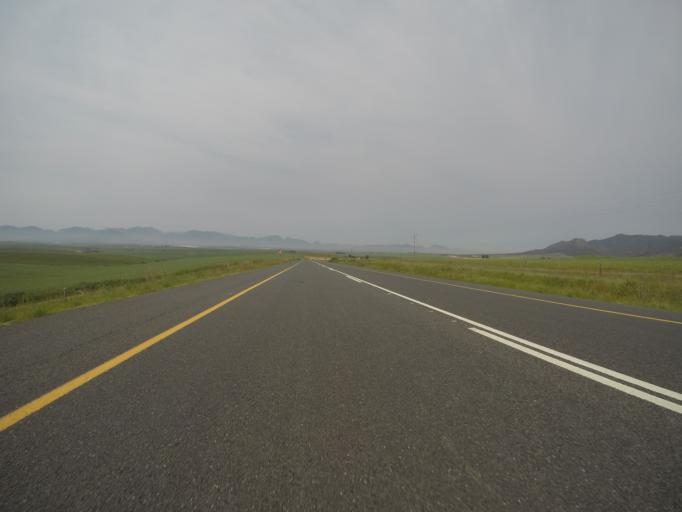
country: ZA
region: Western Cape
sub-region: West Coast District Municipality
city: Malmesbury
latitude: -33.5372
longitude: 18.8560
